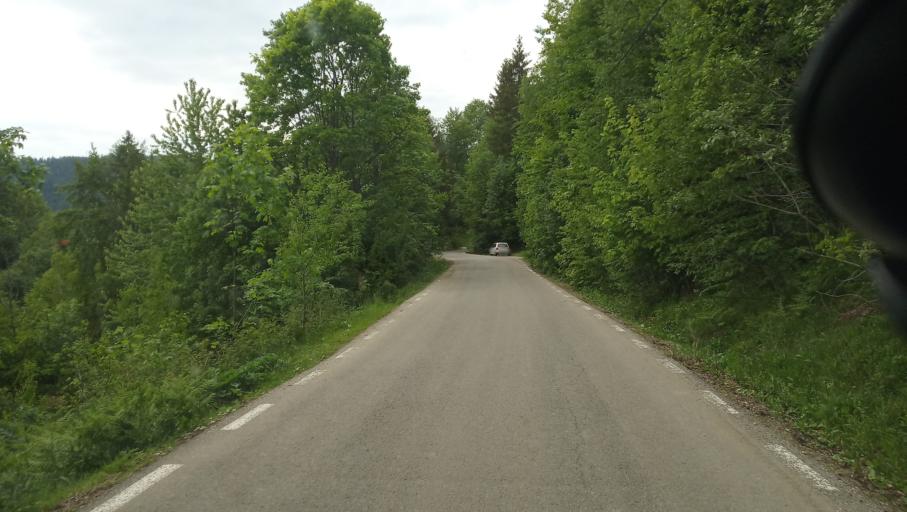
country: RO
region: Alba
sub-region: Comuna Horea
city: Horea
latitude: 46.5063
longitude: 22.8970
